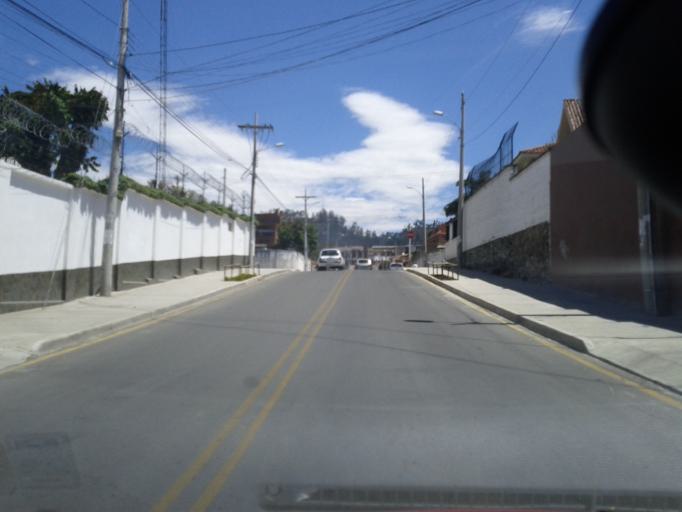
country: EC
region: Azuay
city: Cuenca
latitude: -2.9077
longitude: -79.0096
